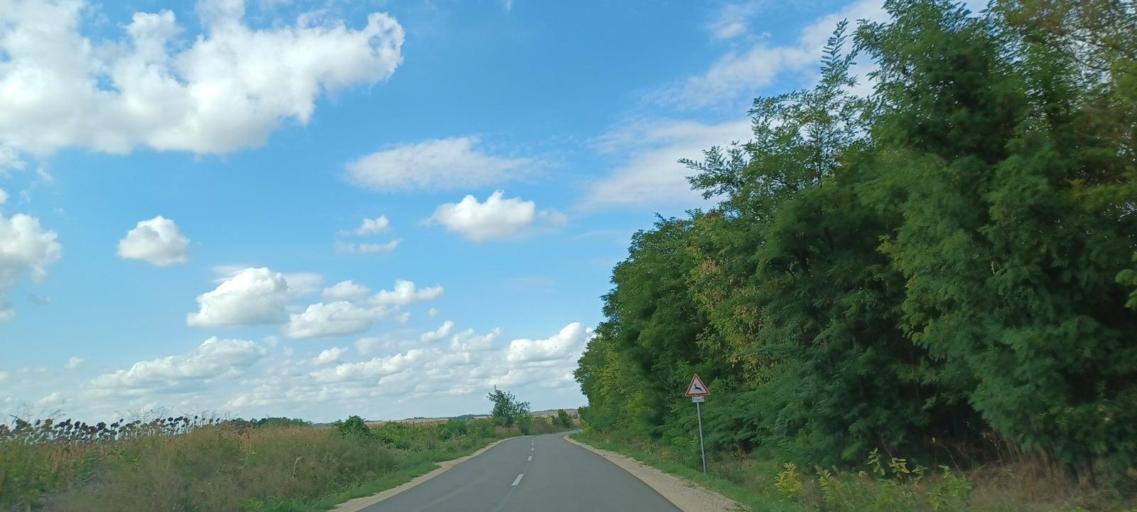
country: HU
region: Tolna
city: Zomba
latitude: 46.4334
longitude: 18.6072
